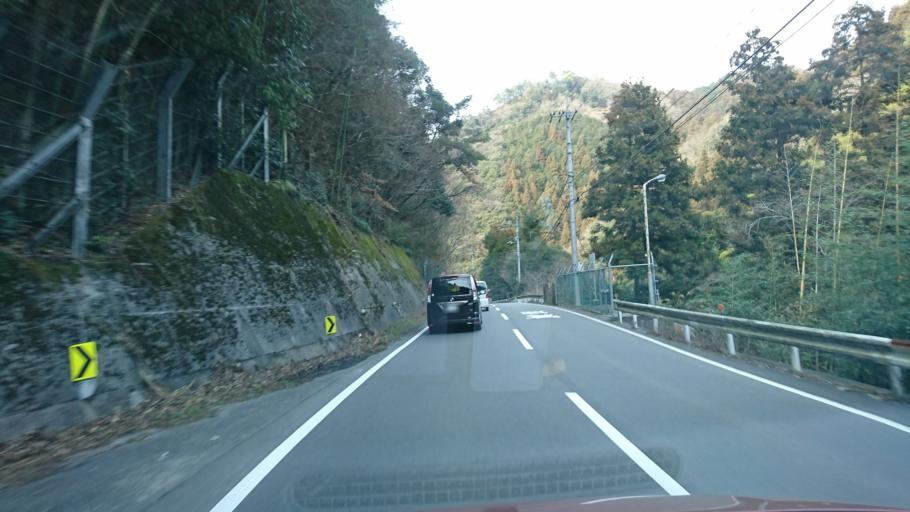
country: JP
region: Ehime
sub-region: Shikoku-chuo Shi
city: Matsuyama
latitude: 33.8972
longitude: 132.8568
